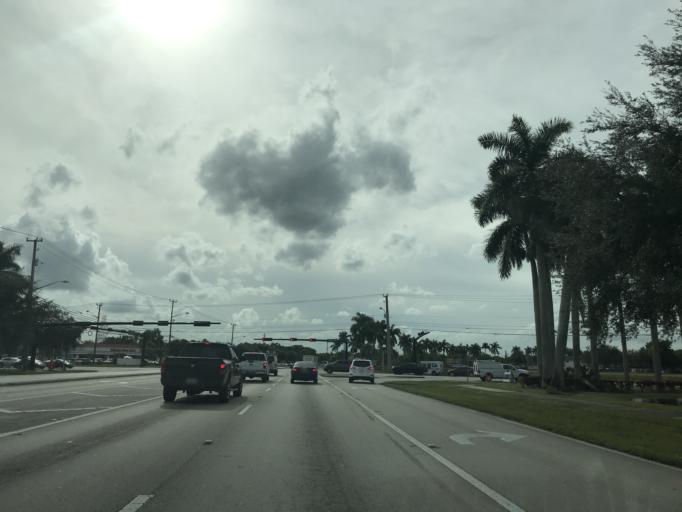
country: US
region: Florida
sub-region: Broward County
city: Coconut Creek
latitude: 26.2561
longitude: -80.1946
